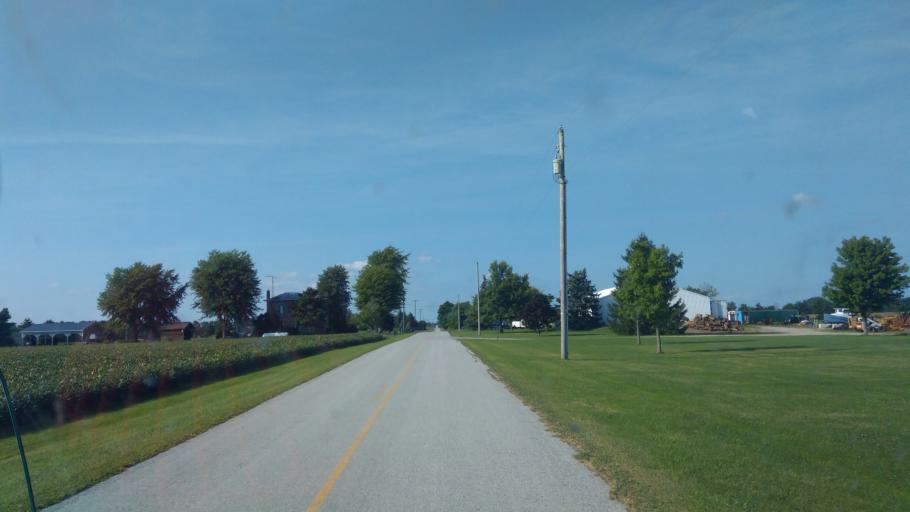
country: US
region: Ohio
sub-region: Hardin County
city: Forest
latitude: 40.7429
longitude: -83.5763
